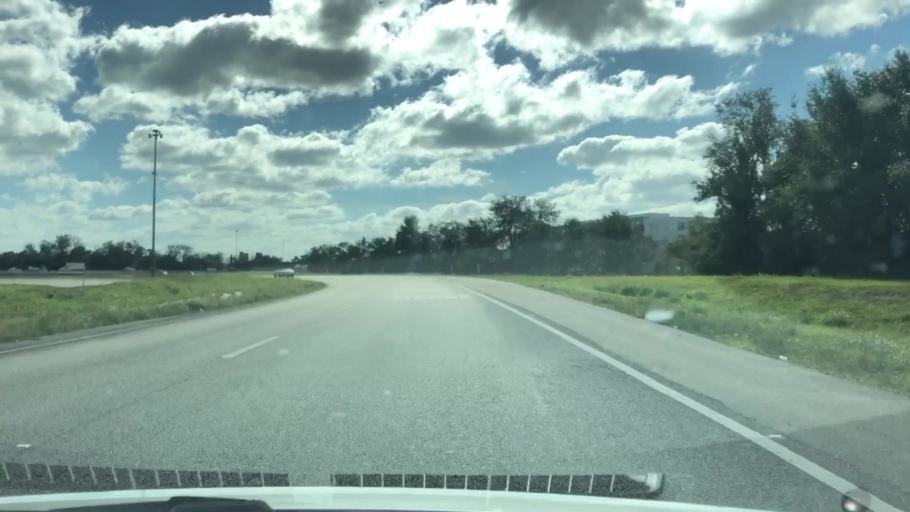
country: US
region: Florida
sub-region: Seminole County
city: Heathrow
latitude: 28.7847
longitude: -81.3543
